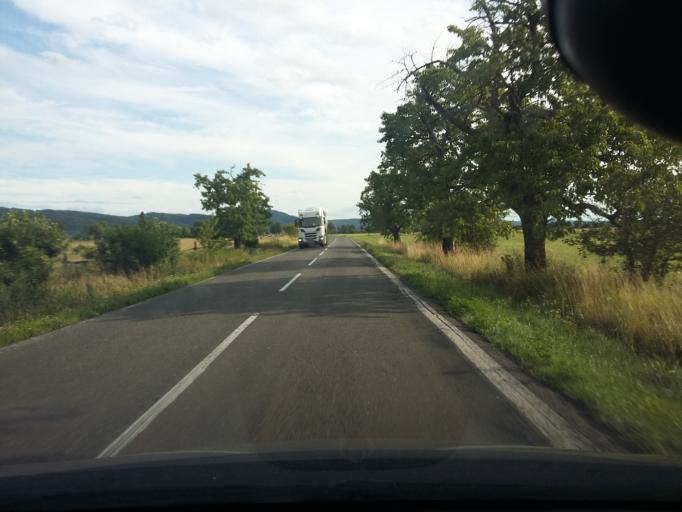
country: SK
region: Bratislavsky
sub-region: Okres Malacky
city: Malacky
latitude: 48.4137
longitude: 17.1567
